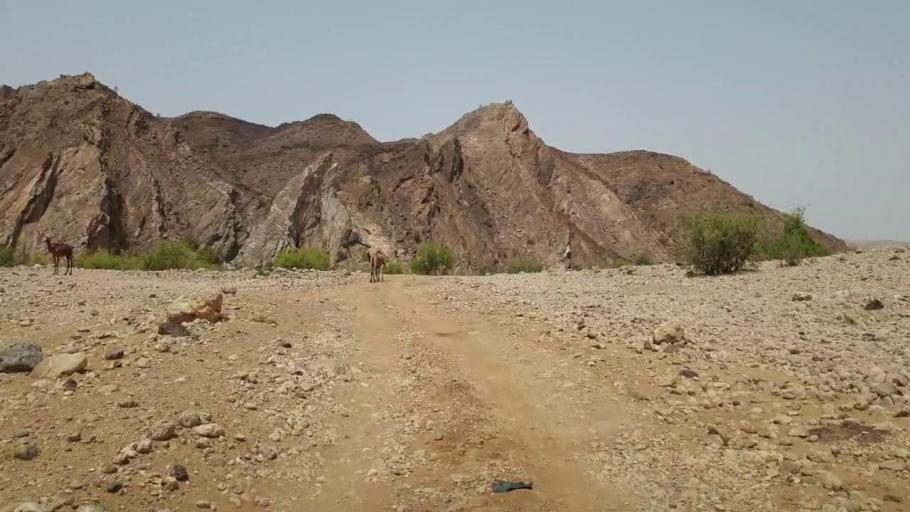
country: PK
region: Sindh
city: Sann
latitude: 25.8830
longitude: 67.9238
